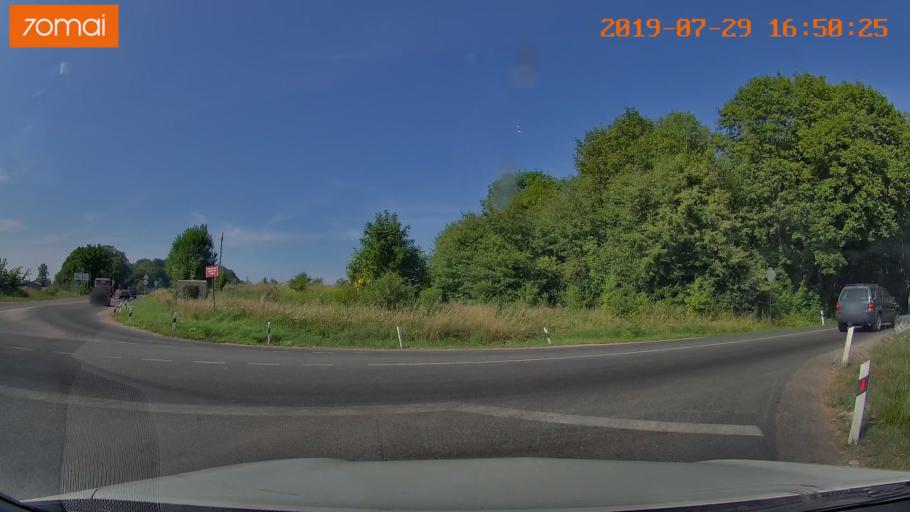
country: RU
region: Kaliningrad
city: Primorsk
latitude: 54.8025
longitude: 20.0564
